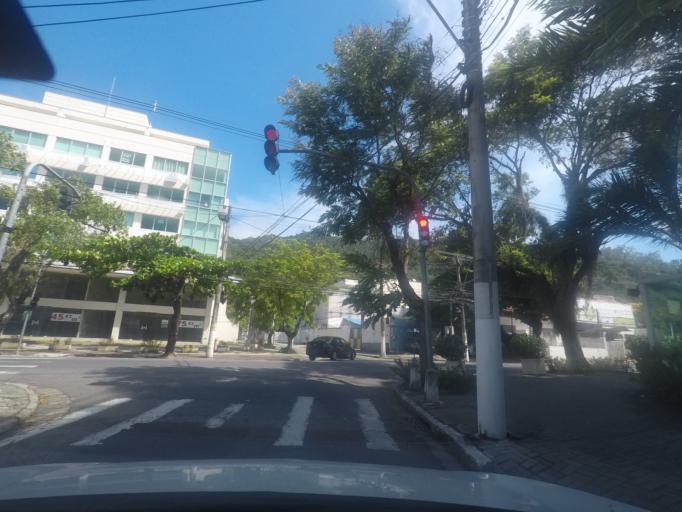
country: BR
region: Rio de Janeiro
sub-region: Niteroi
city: Niteroi
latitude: -22.9176
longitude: -43.0861
